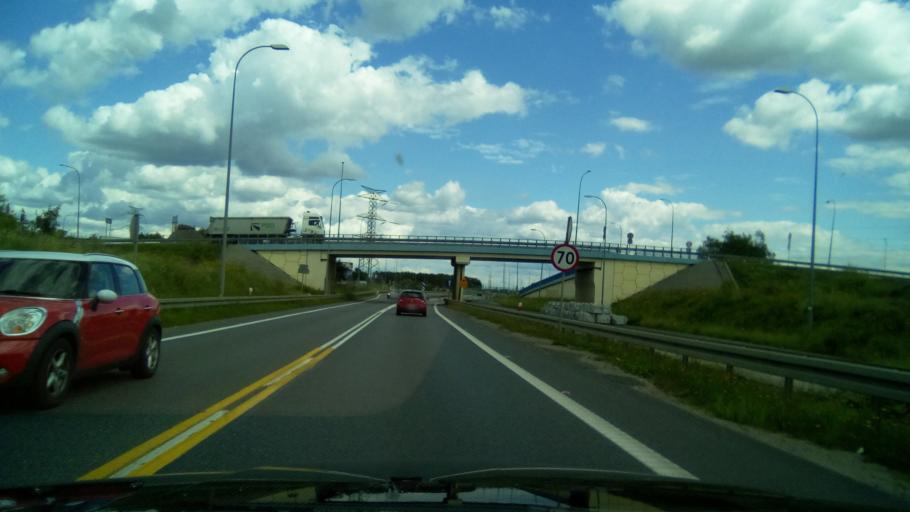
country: PL
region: Kujawsko-Pomorskie
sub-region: Powiat bydgoski
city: Biale Blota
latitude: 53.0835
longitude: 17.8695
